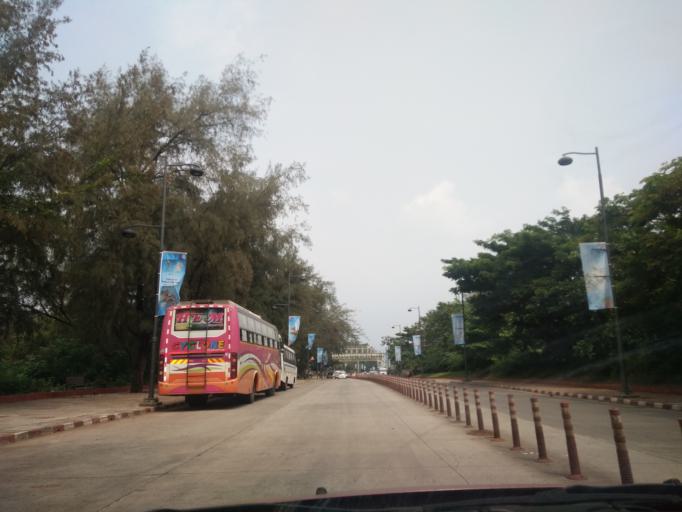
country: IN
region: Goa
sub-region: North Goa
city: Panaji
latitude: 15.4789
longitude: 73.8084
